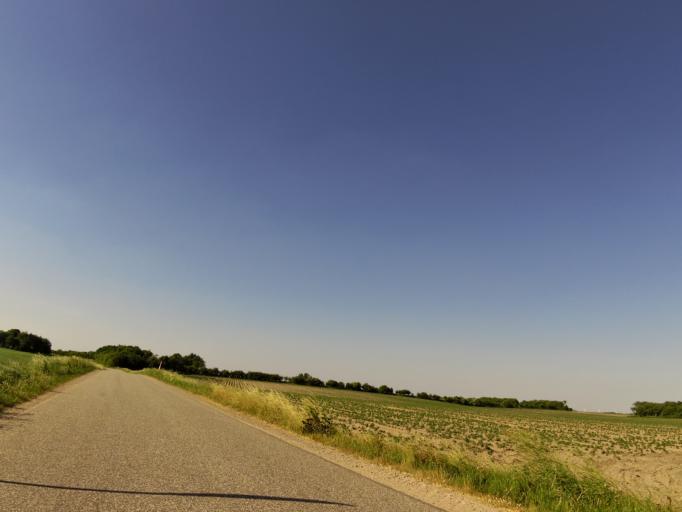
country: DK
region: Central Jutland
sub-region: Holstebro Kommune
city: Vinderup
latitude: 56.4493
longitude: 8.6923
